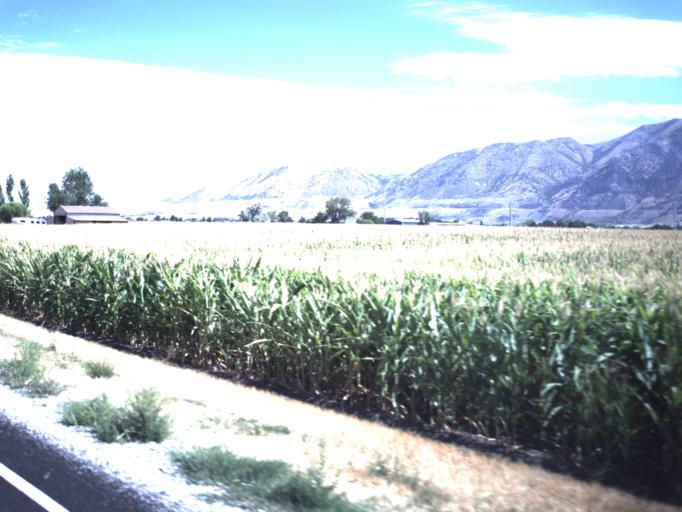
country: US
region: Utah
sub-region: Box Elder County
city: Elwood
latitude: 41.6602
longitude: -112.1405
